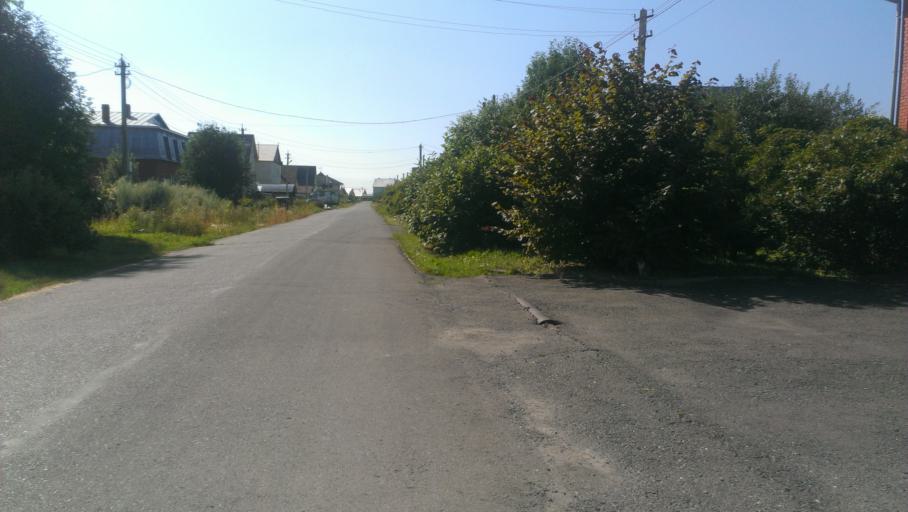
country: RU
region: Altai Krai
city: Novosilikatnyy
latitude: 53.3700
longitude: 83.6574
